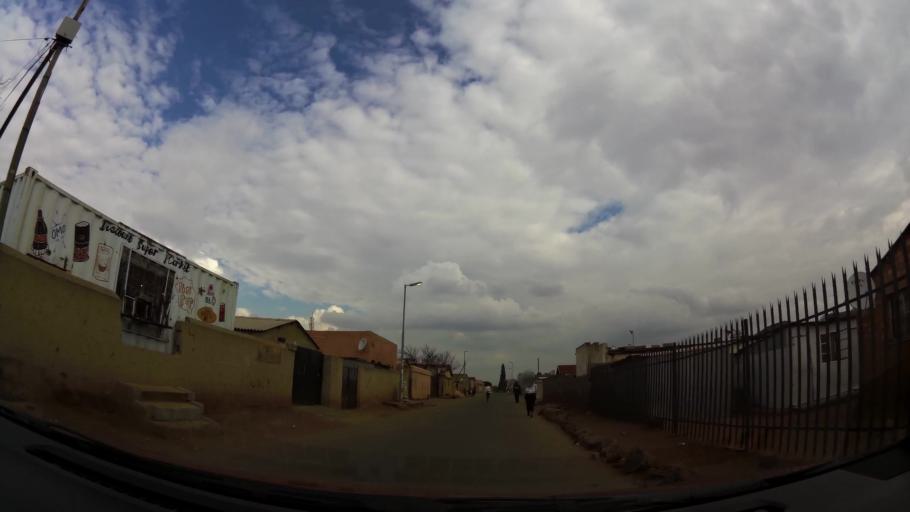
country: ZA
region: Gauteng
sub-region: City of Johannesburg Metropolitan Municipality
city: Soweto
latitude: -26.2433
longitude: 27.8554
